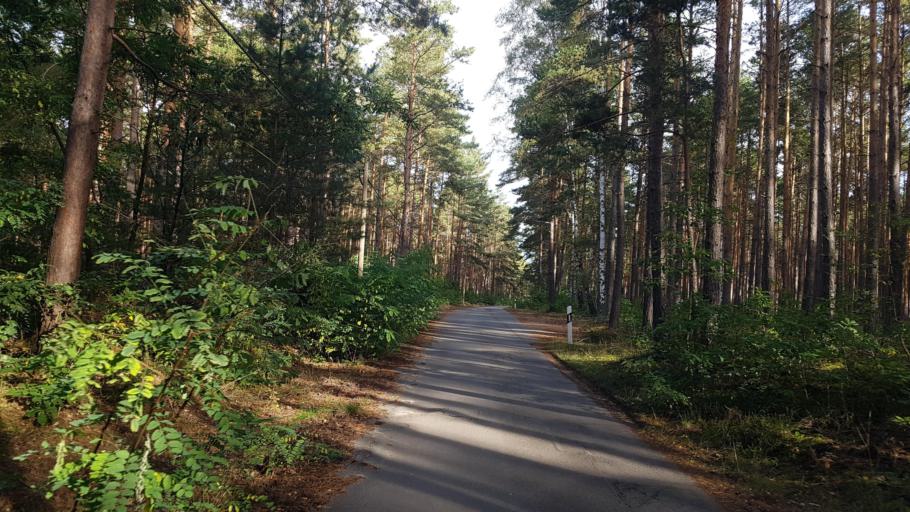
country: DE
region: Brandenburg
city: Hohenbucko
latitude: 51.8216
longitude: 13.5303
